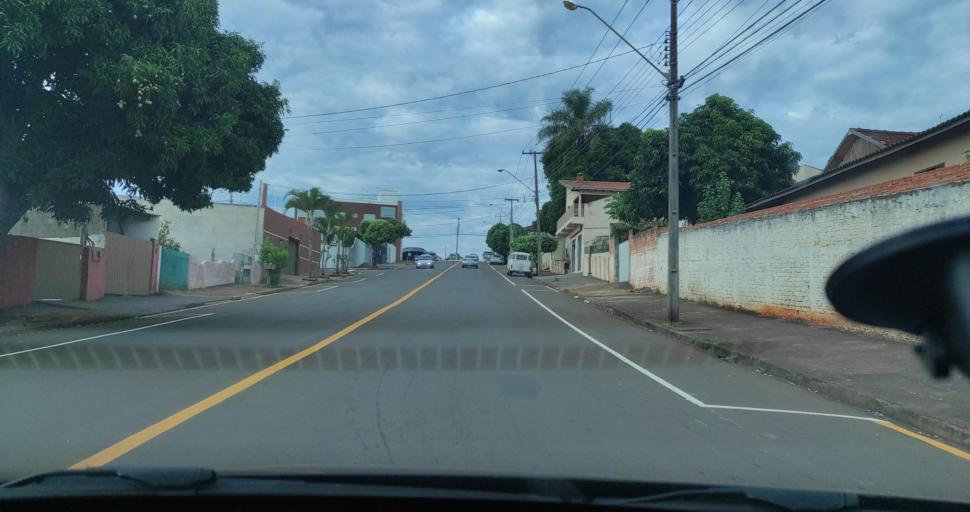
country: BR
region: Parana
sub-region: Ibipora
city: Ibipora
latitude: -23.2662
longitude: -51.0447
